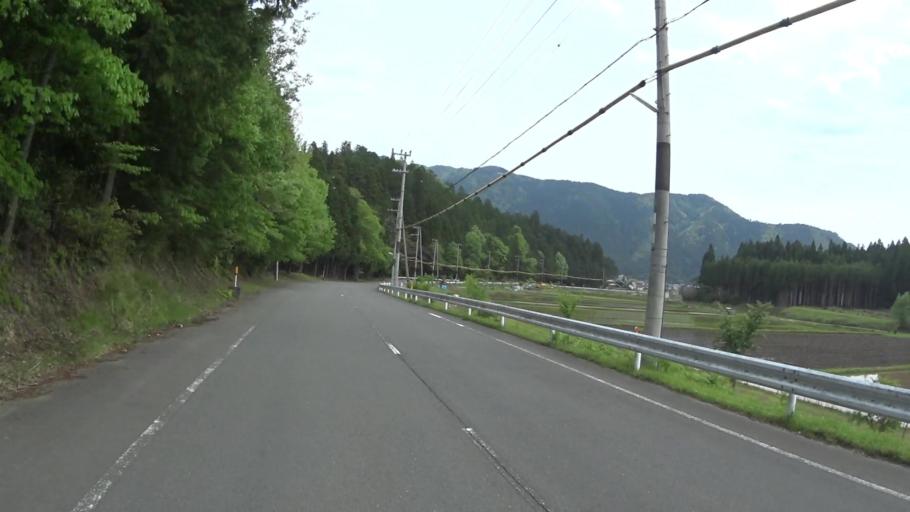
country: JP
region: Kyoto
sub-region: Kyoto-shi
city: Kamigyo-ku
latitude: 35.1858
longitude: 135.6541
